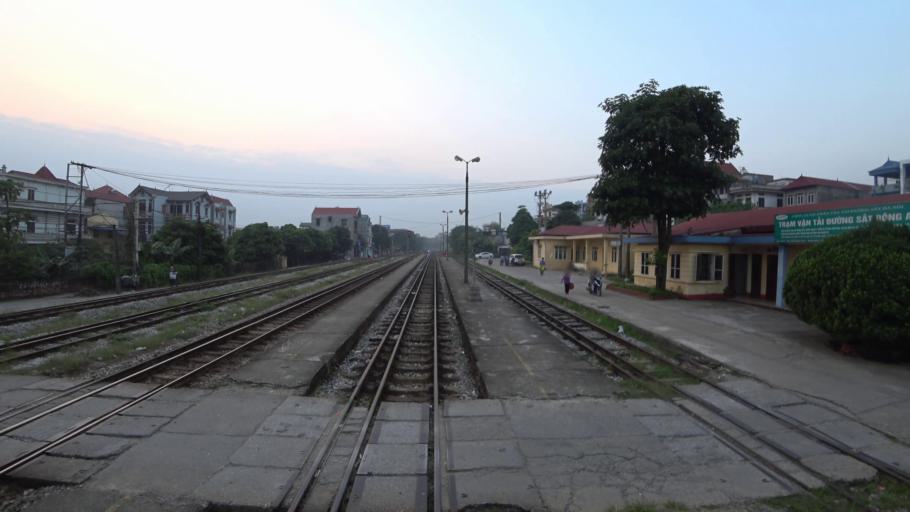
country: VN
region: Ha Noi
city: Dong Anh
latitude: 21.1596
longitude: 105.8471
